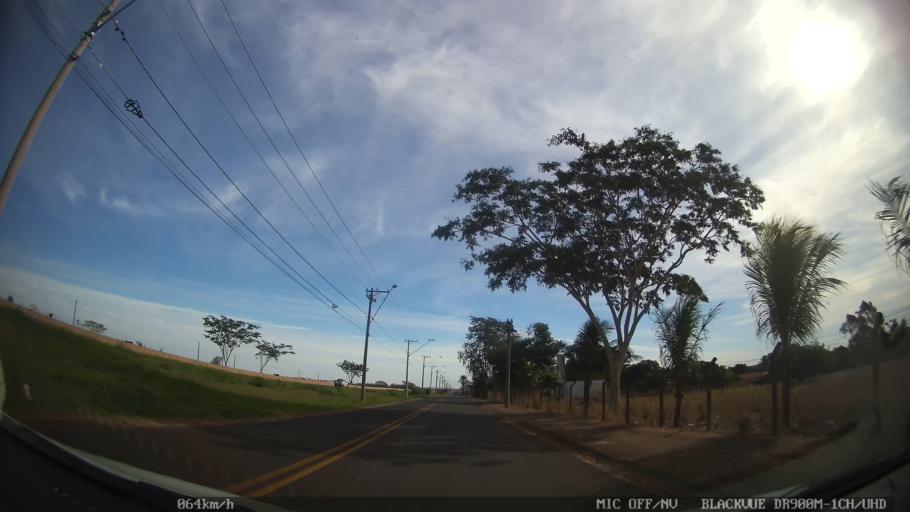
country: BR
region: Sao Paulo
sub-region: Sao Jose Do Rio Preto
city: Sao Jose do Rio Preto
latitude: -20.7918
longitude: -49.3027
